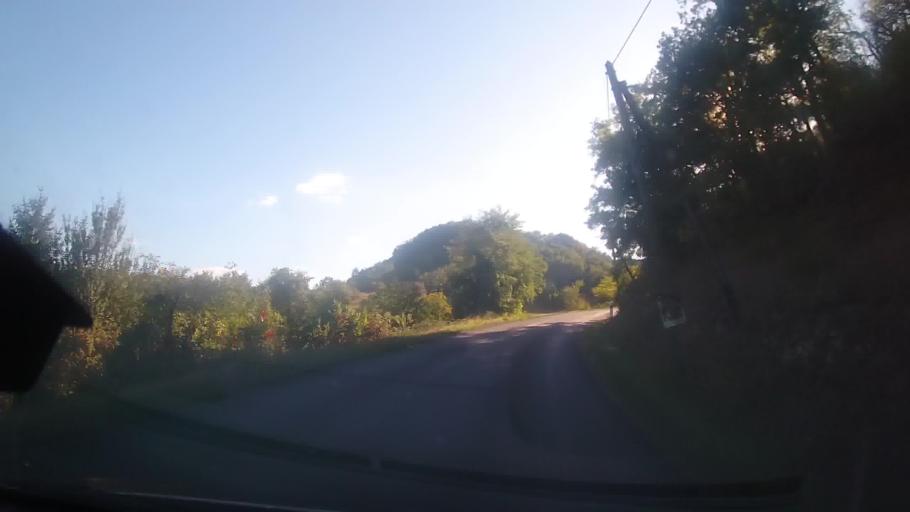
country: FR
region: Aquitaine
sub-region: Departement de la Dordogne
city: Cenac-et-Saint-Julien
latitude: 44.7984
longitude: 1.1962
